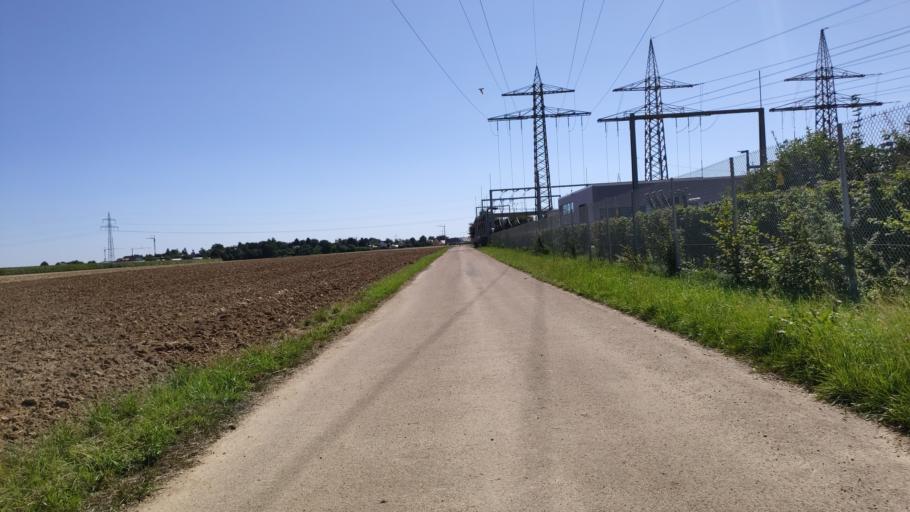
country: DE
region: Bavaria
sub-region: Swabia
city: Oberottmarshausen
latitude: 48.2400
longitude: 10.8411
